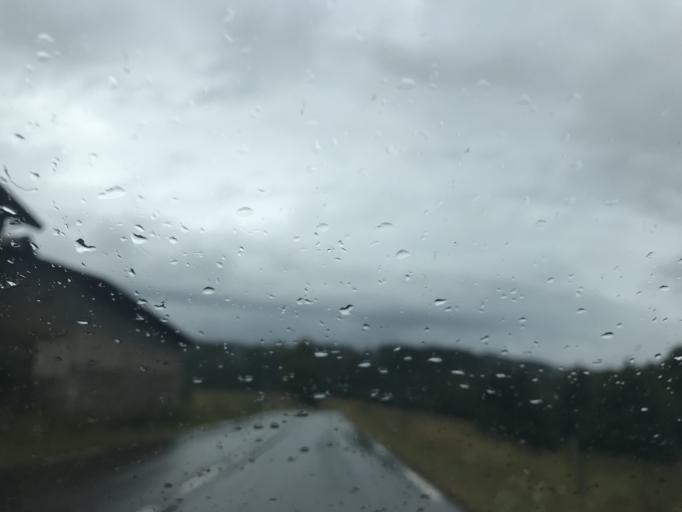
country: FR
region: Auvergne
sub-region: Departement du Puy-de-Dome
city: Job
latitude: 45.5840
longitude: 3.7315
